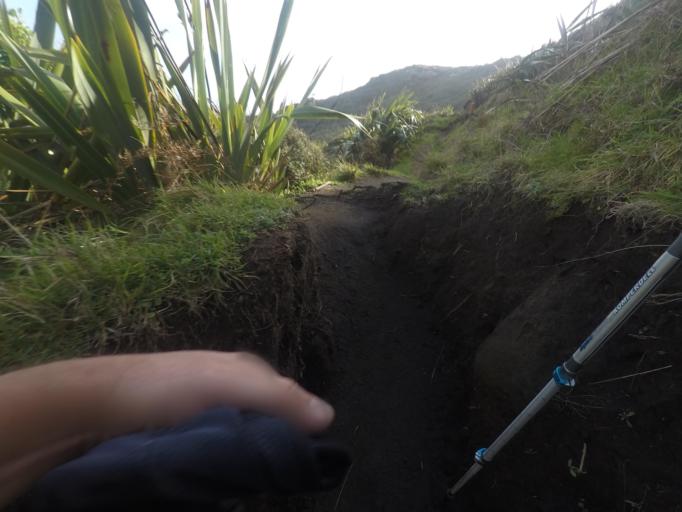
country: NZ
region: Auckland
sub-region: Auckland
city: Muriwai Beach
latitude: -36.8668
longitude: 174.4366
